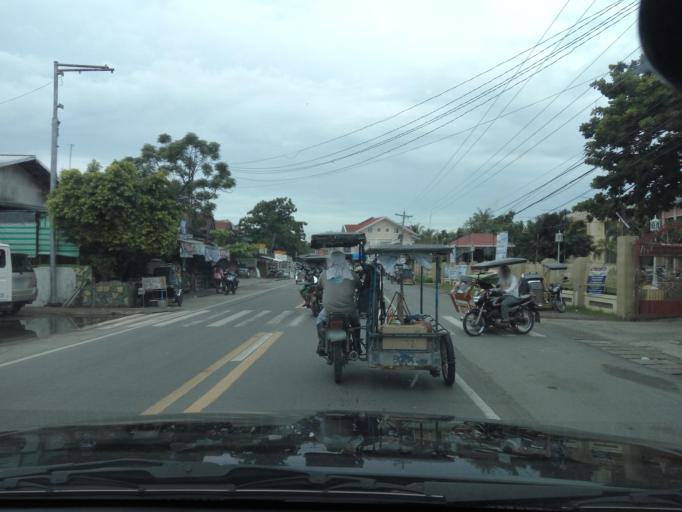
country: PH
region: Central Luzon
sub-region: Province of Nueva Ecija
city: Concepcion
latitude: 15.4498
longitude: 120.7932
